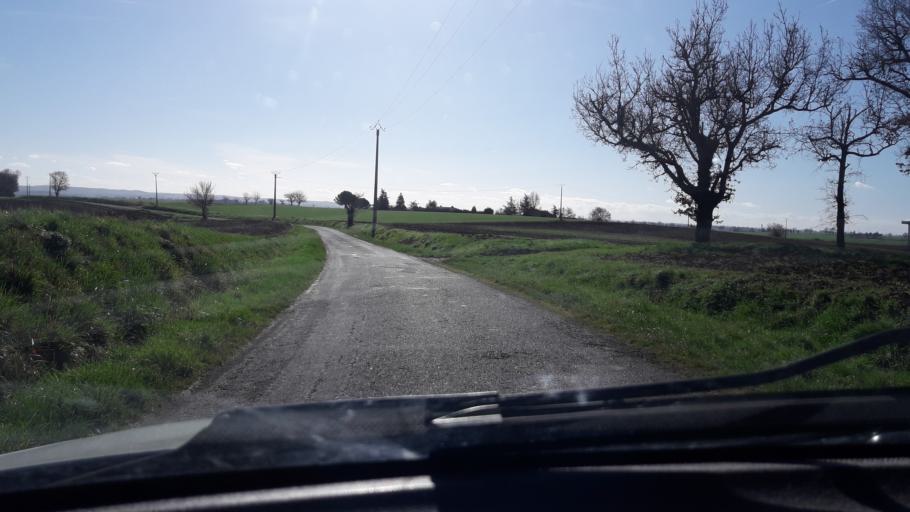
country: FR
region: Midi-Pyrenees
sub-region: Departement du Gers
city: Gimont
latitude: 43.6505
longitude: 1.0136
